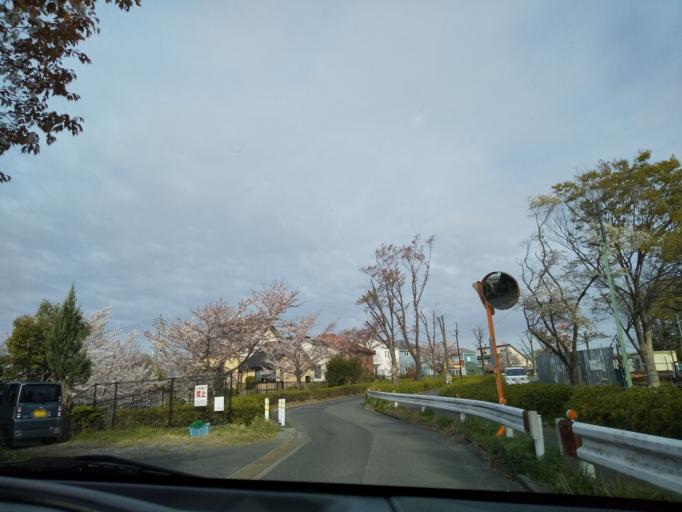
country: JP
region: Tokyo
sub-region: Machida-shi
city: Machida
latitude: 35.5929
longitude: 139.3905
